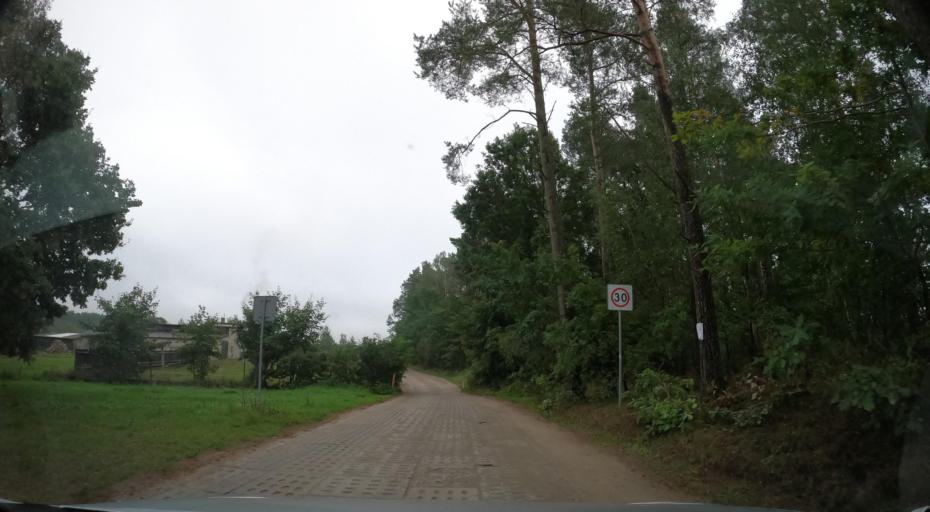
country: PL
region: Pomeranian Voivodeship
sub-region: Powiat kartuski
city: Chwaszczyno
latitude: 54.4220
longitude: 18.4164
